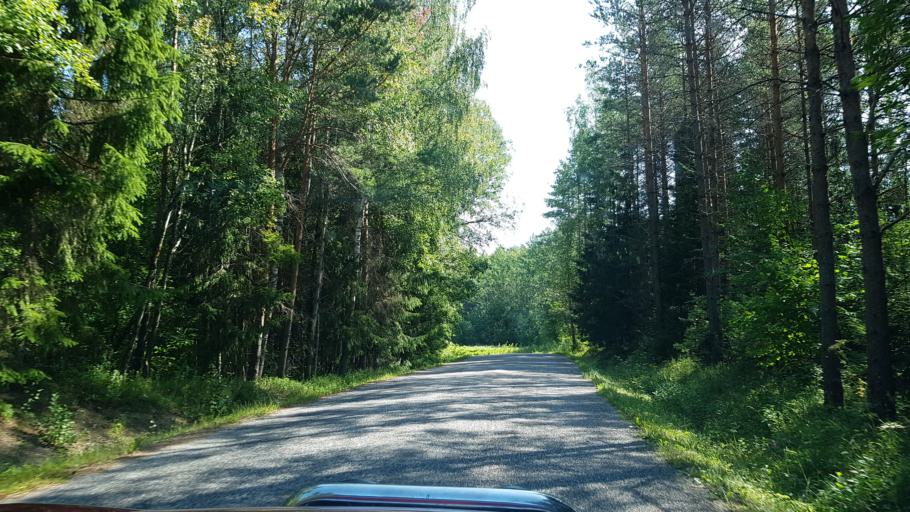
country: EE
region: Vorumaa
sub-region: Voru linn
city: Voru
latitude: 57.7081
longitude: 27.1667
